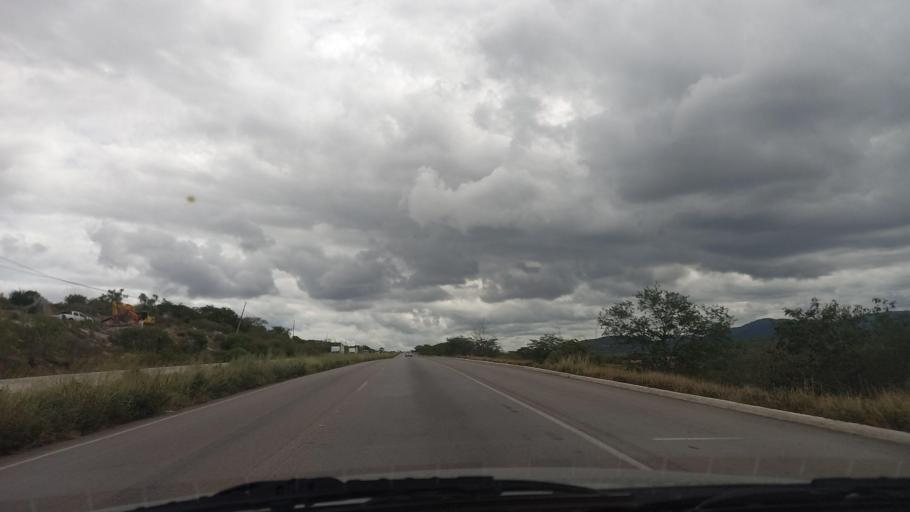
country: BR
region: Pernambuco
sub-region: Caruaru
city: Caruaru
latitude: -8.3224
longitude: -36.0946
